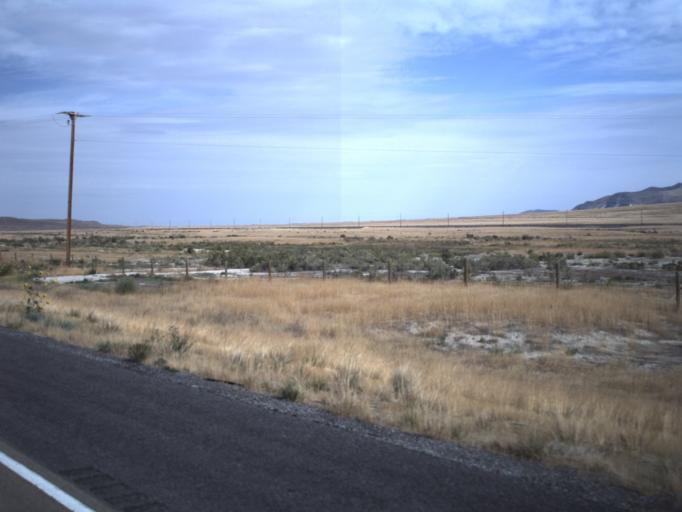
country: US
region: Utah
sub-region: Tooele County
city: Grantsville
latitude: 40.7979
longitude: -112.8452
